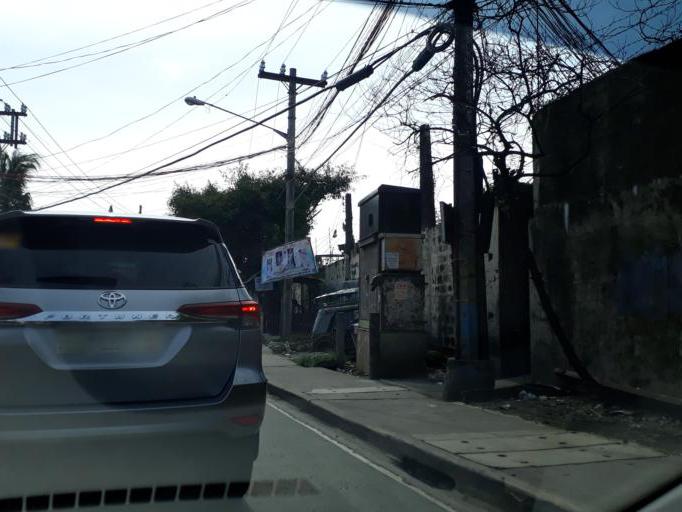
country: PH
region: Metro Manila
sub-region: Caloocan City
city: Niugan
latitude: 14.6679
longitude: 120.9646
